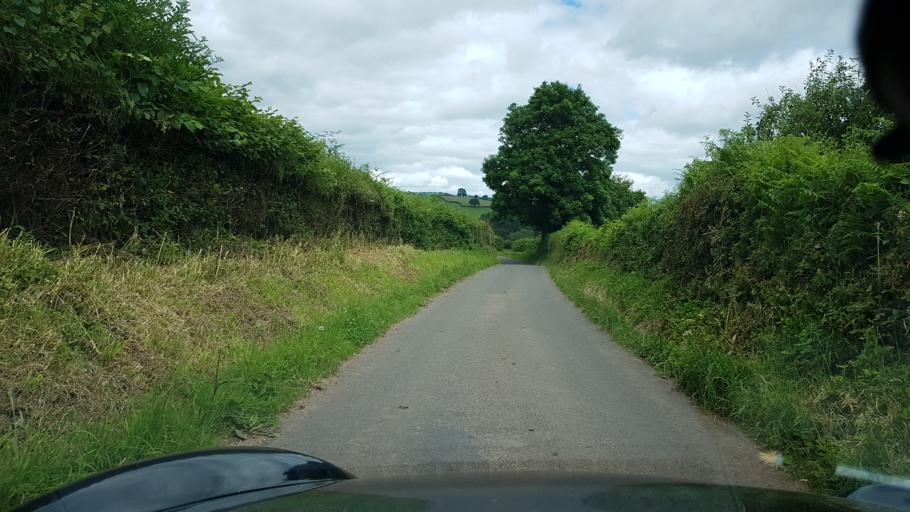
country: GB
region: Wales
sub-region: Monmouthshire
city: Llanarth
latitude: 51.8486
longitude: -2.8994
